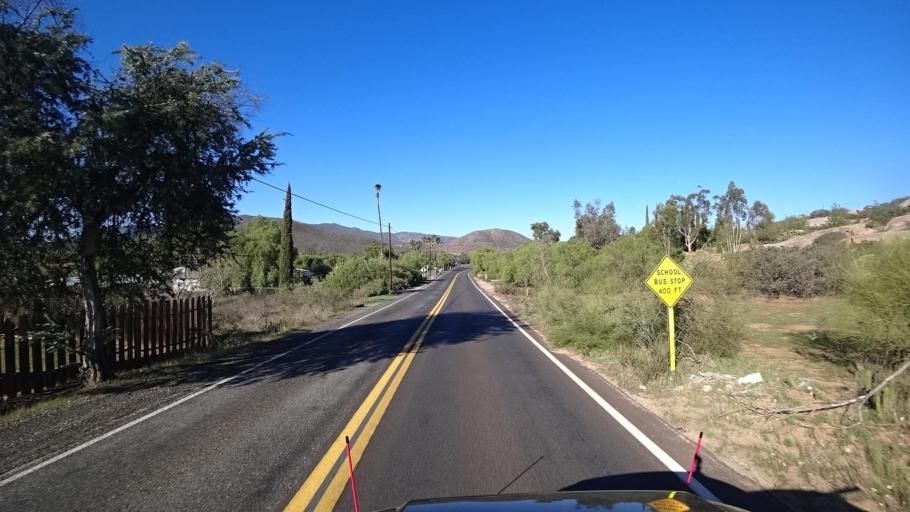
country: MX
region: Baja California
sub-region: Tijuana
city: Villa del Campo
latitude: 32.6216
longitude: -116.7604
